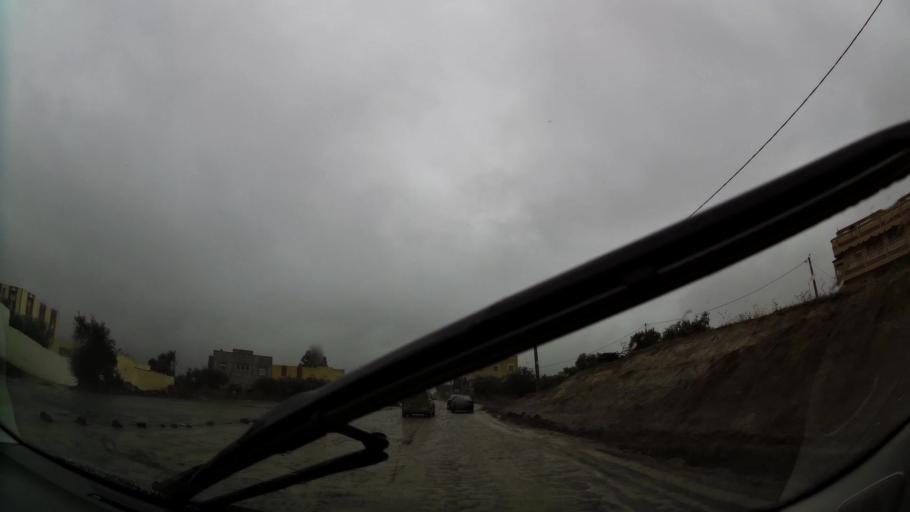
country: MA
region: Oriental
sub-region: Nador
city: Midar
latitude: 34.8725
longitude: -3.7259
